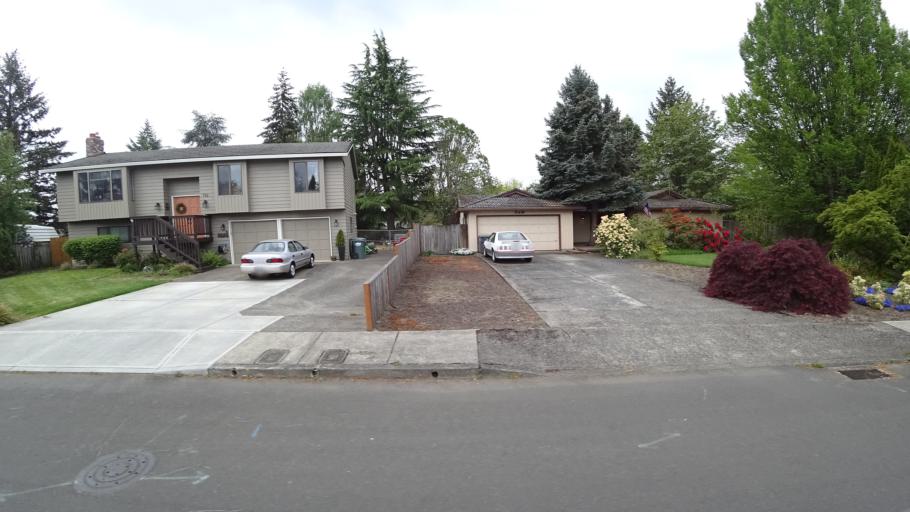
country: US
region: Oregon
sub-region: Washington County
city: Hillsboro
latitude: 45.5336
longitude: -122.9788
